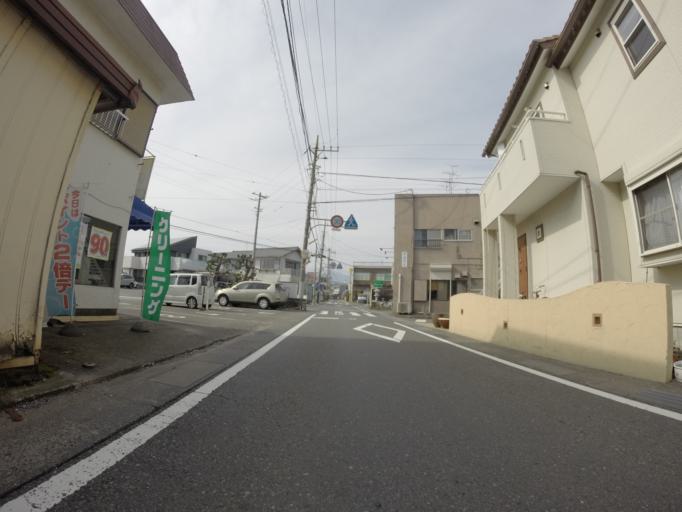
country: JP
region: Shizuoka
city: Numazu
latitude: 35.0832
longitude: 138.8710
